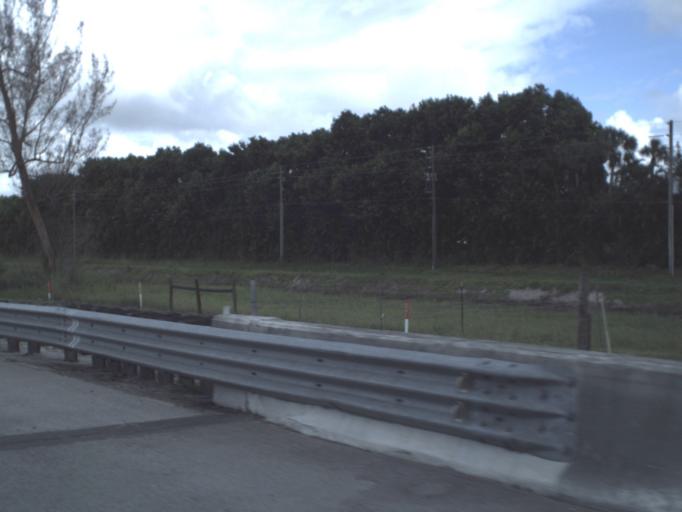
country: US
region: Florida
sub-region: Palm Beach County
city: Kings Point
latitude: 26.4241
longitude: -80.1715
